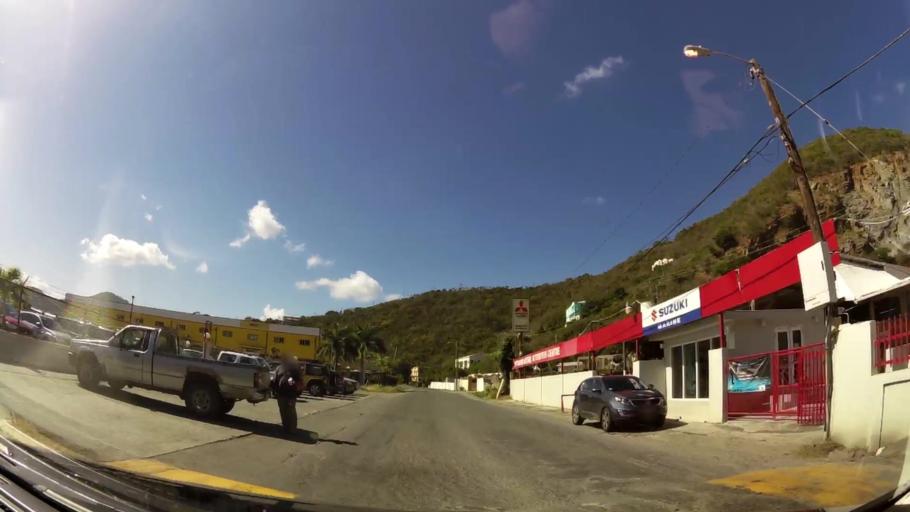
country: VG
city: Tortola
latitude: 18.4194
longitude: -64.5982
